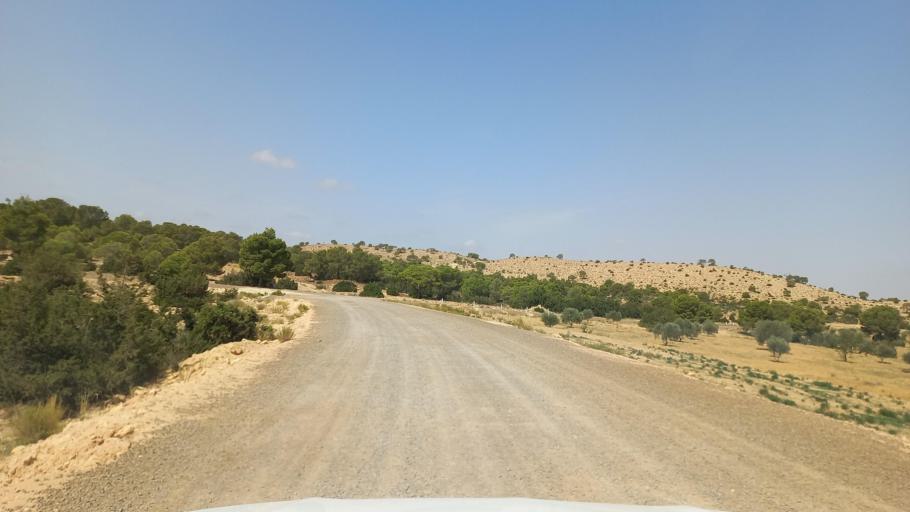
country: TN
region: Al Qasrayn
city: Sbiba
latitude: 35.3925
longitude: 8.9503
